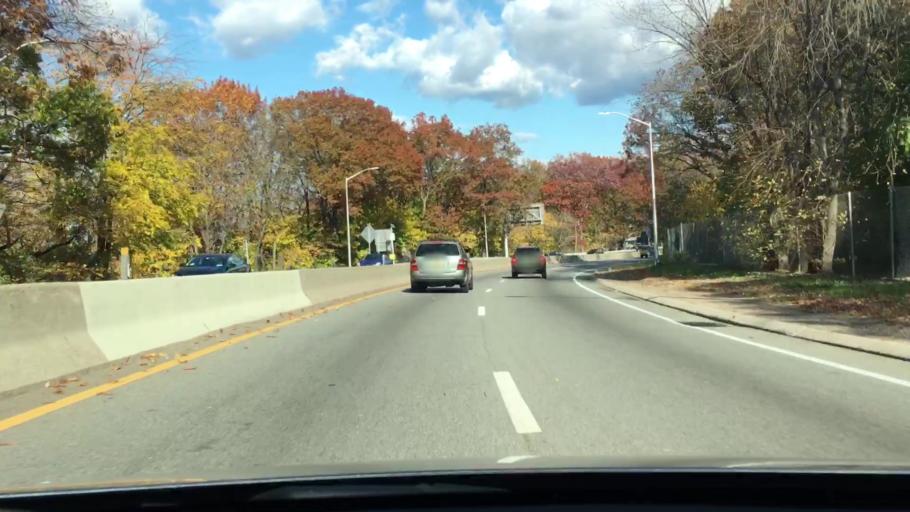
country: US
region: New York
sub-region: Queens County
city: Borough of Queens
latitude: 40.7014
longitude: -73.8680
